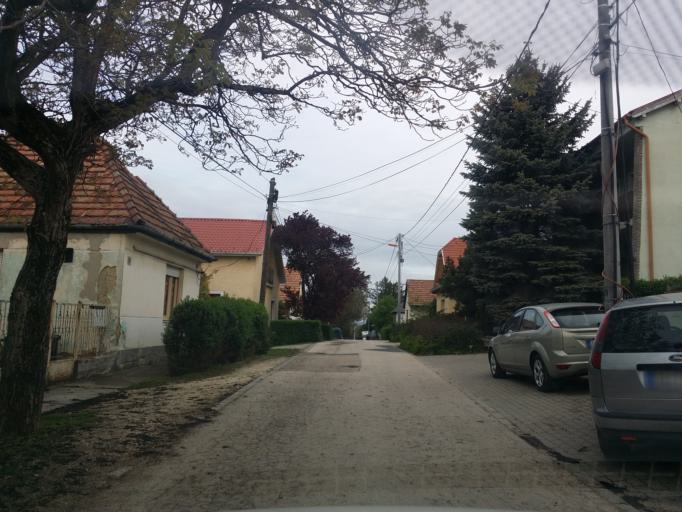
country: HU
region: Pest
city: Biatorbagy
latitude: 47.4755
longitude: 18.8327
